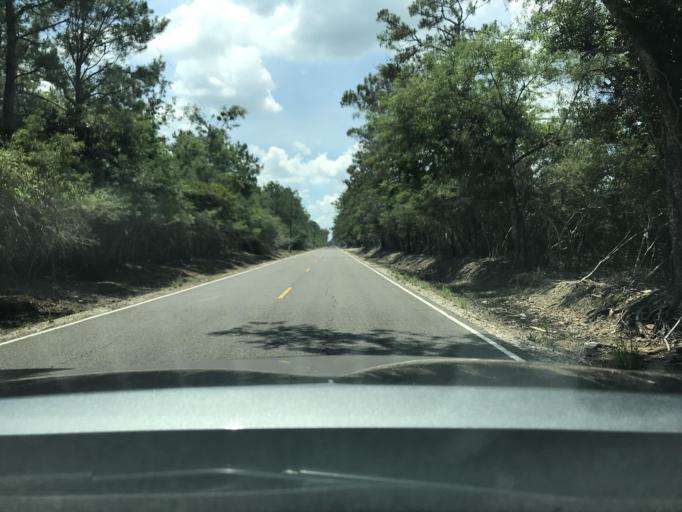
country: US
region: Louisiana
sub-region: Calcasieu Parish
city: Moss Bluff
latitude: 30.3298
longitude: -93.1395
